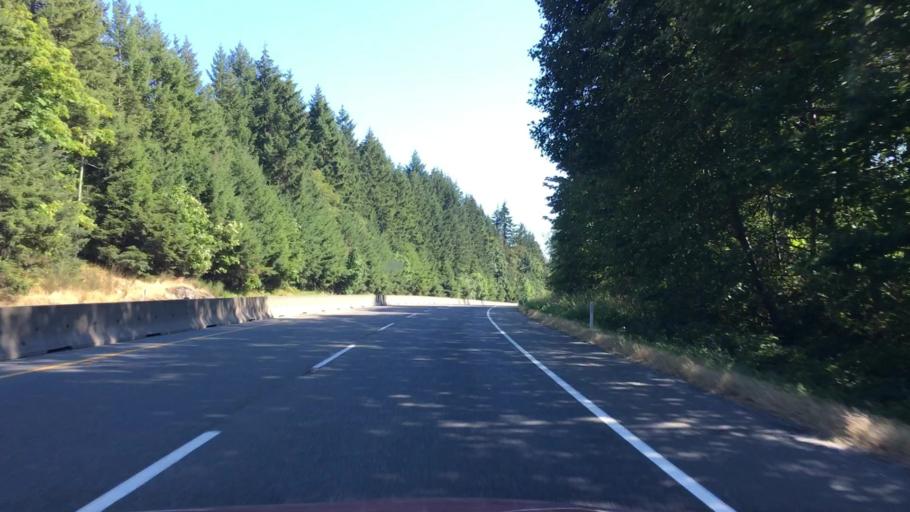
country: CA
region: British Columbia
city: North Cowichan
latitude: 48.8440
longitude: -123.7185
